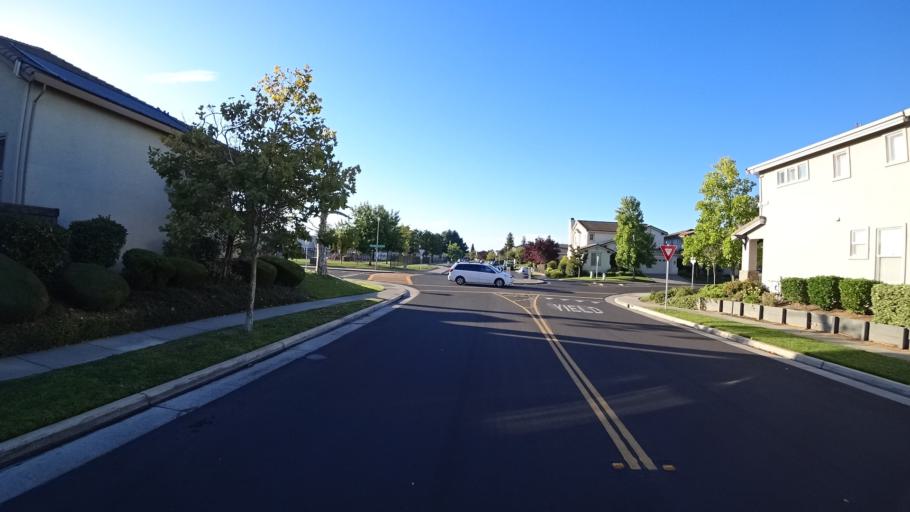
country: US
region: California
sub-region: Sacramento County
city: Laguna
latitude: 38.3980
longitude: -121.4752
